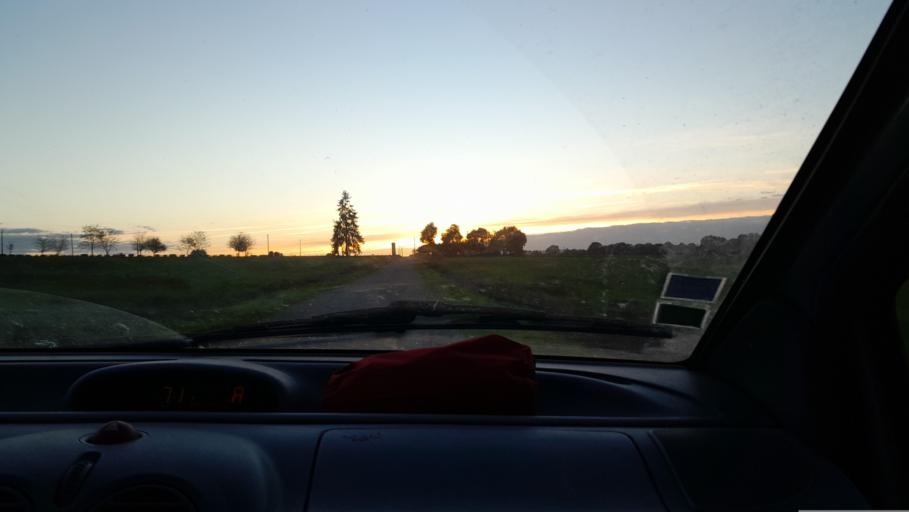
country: FR
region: Brittany
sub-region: Departement d'Ille-et-Vilaine
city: La Guerche-de-Bretagne
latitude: 47.8929
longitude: -1.1657
